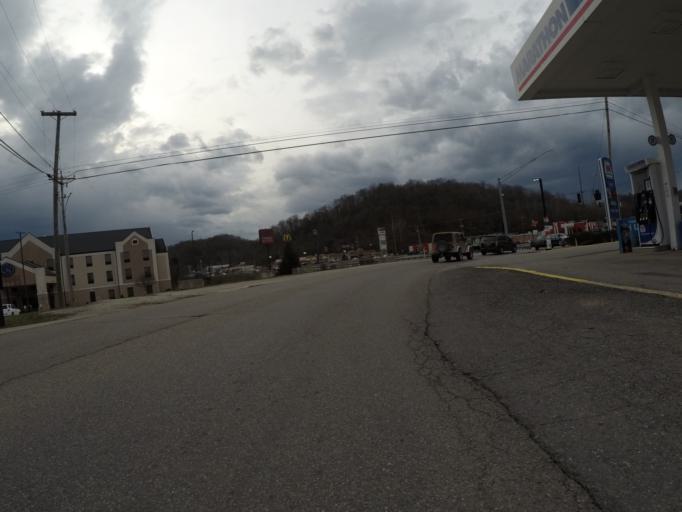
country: US
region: Ohio
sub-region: Lawrence County
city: Burlington
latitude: 38.4190
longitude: -82.5033
